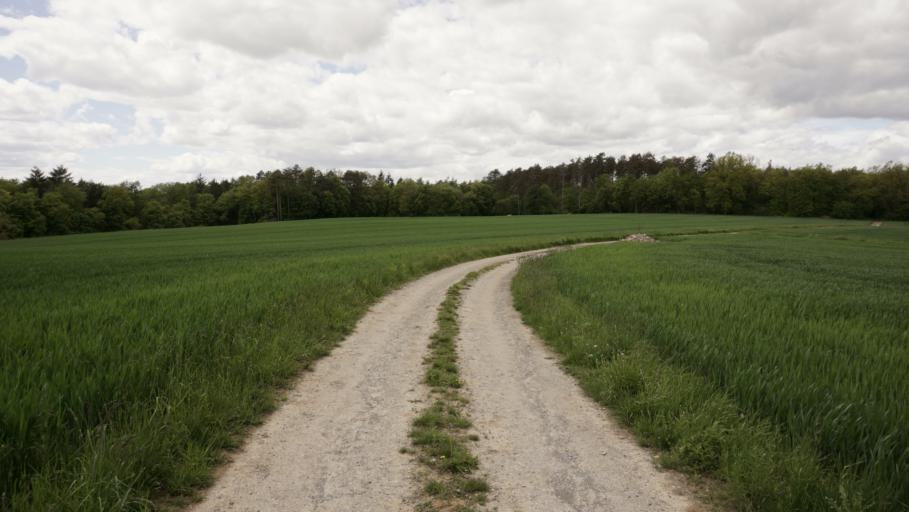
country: DE
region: Baden-Wuerttemberg
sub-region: Karlsruhe Region
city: Mosbach
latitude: 49.3674
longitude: 9.1725
